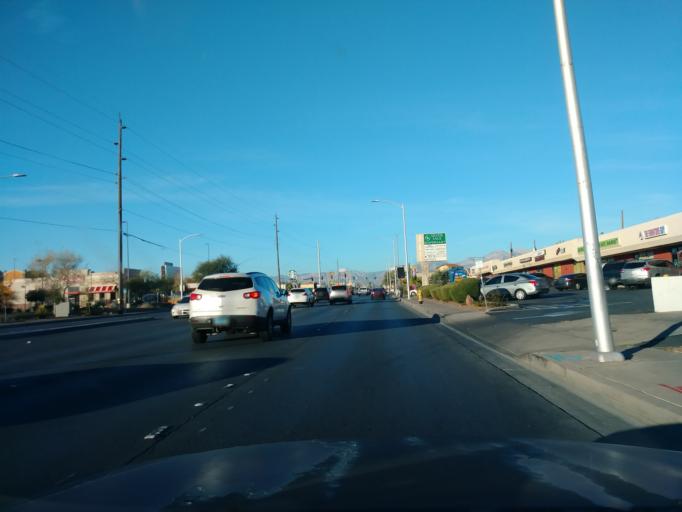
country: US
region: Nevada
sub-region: Clark County
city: Spring Valley
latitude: 36.1592
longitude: -115.2035
